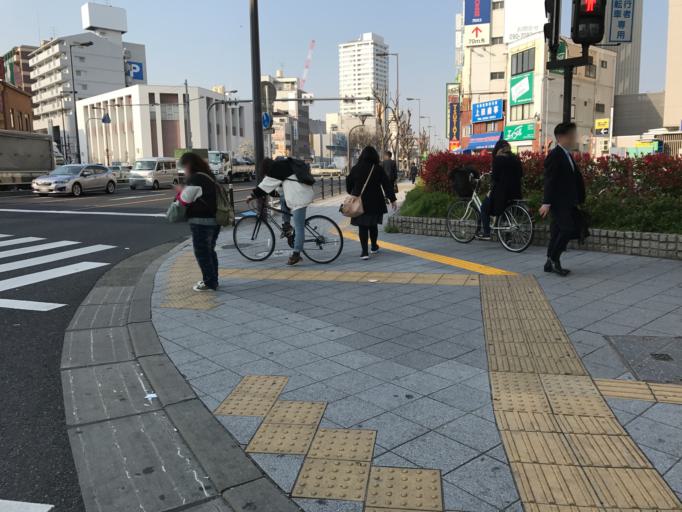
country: JP
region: Osaka
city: Osaka-shi
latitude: 34.6938
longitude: 135.4751
